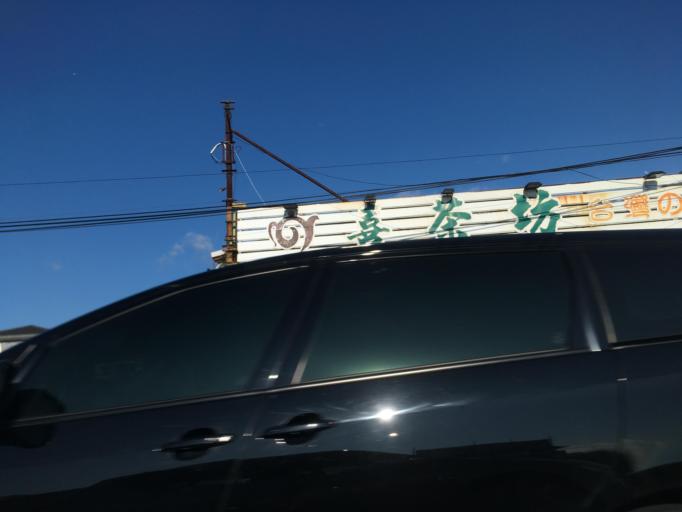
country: TW
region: Taiwan
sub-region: Yilan
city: Yilan
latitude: 24.8597
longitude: 121.8267
